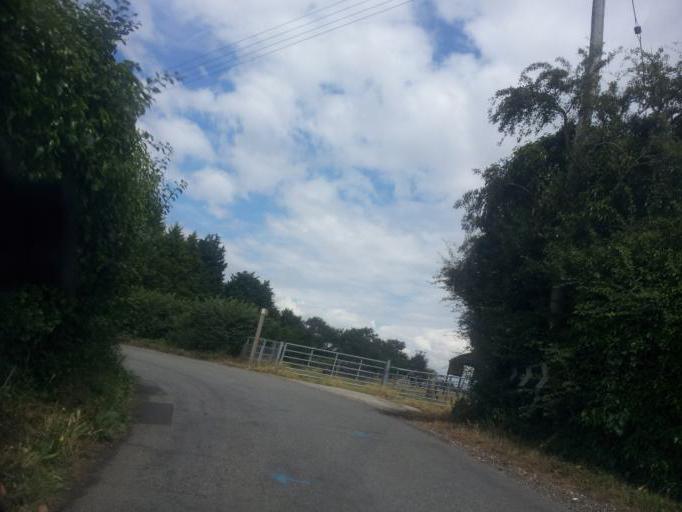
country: GB
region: England
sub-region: Kent
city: Newington
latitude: 51.3727
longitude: 0.6573
